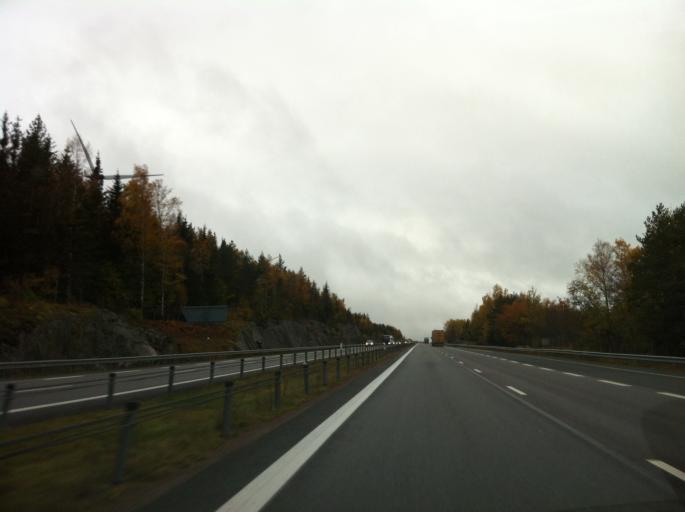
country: SE
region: Joenkoeping
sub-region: Jonkopings Kommun
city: Graenna
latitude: 58.0487
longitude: 14.5037
